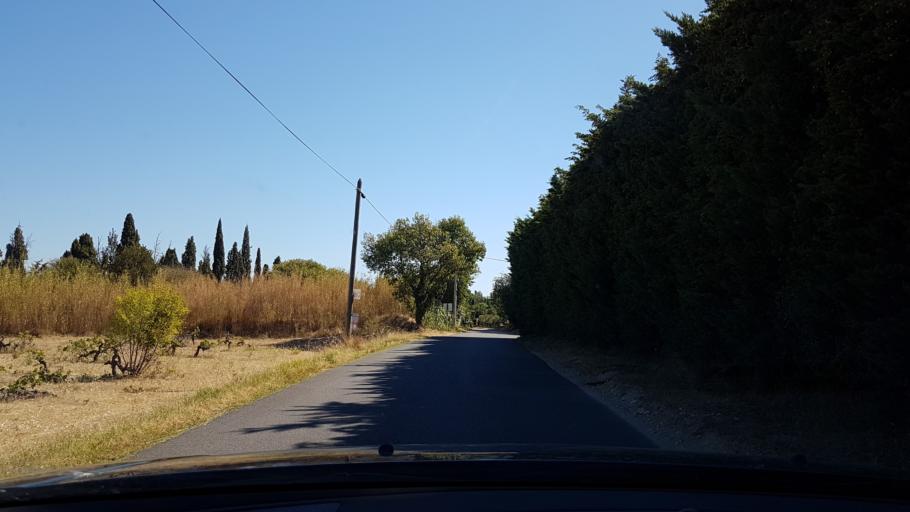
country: FR
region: Provence-Alpes-Cote d'Azur
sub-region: Departement des Bouches-du-Rhone
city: Saint-Remy-de-Provence
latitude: 43.7812
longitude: 4.8587
